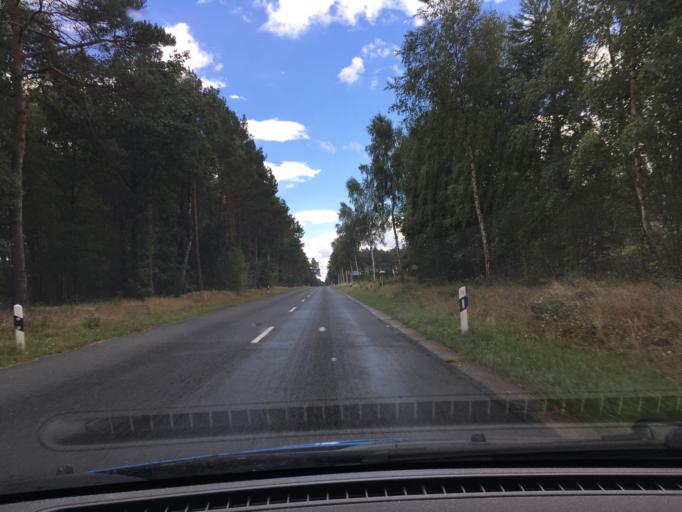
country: DE
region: Lower Saxony
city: Wietzendorf
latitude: 52.9293
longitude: 10.0026
